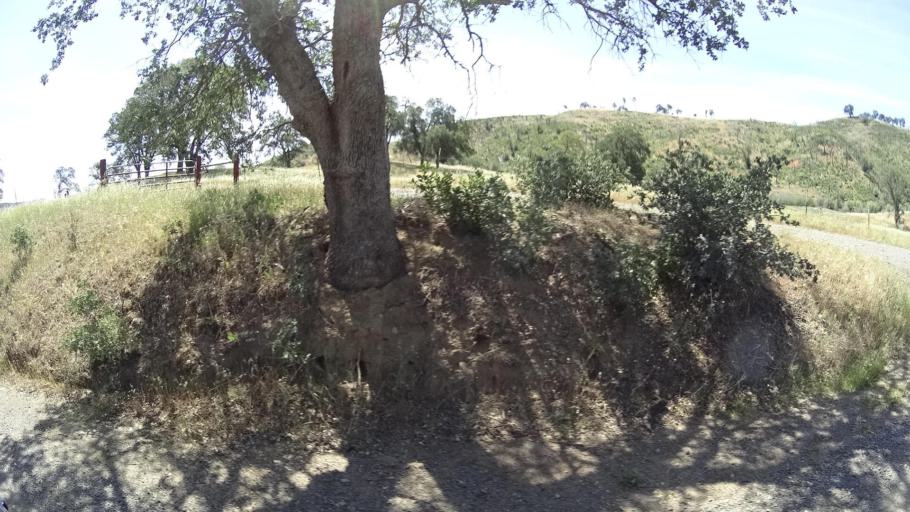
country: US
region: California
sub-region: Lake County
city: Middletown
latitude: 38.7799
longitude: -122.6156
